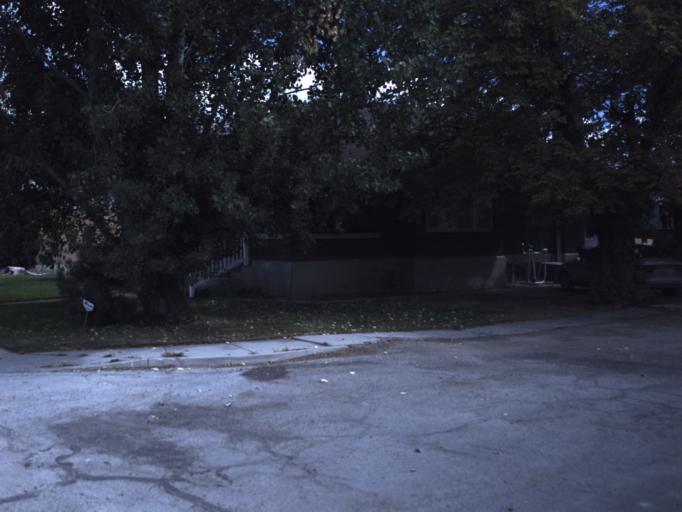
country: US
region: Utah
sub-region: Box Elder County
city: Garland
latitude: 41.7412
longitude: -112.1560
